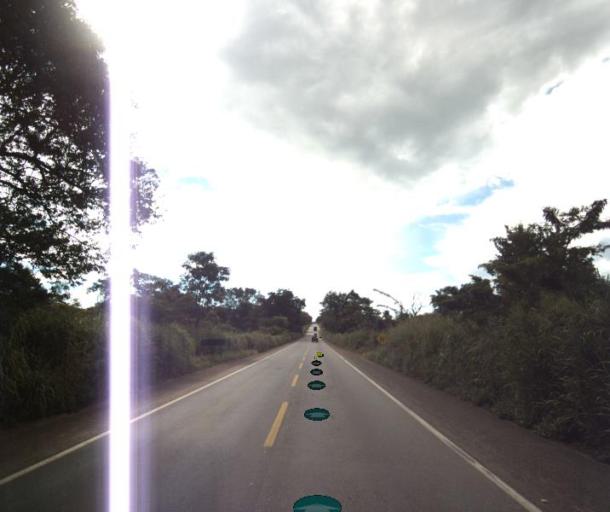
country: BR
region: Goias
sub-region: Jaragua
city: Jaragua
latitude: -15.6734
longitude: -49.3472
